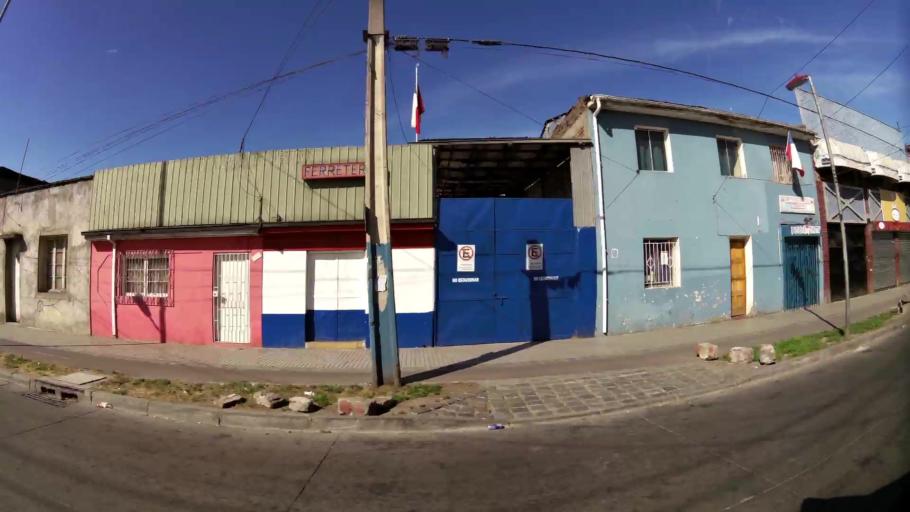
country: CL
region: Santiago Metropolitan
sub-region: Provincia de Santiago
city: Santiago
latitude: -33.4775
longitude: -70.6342
